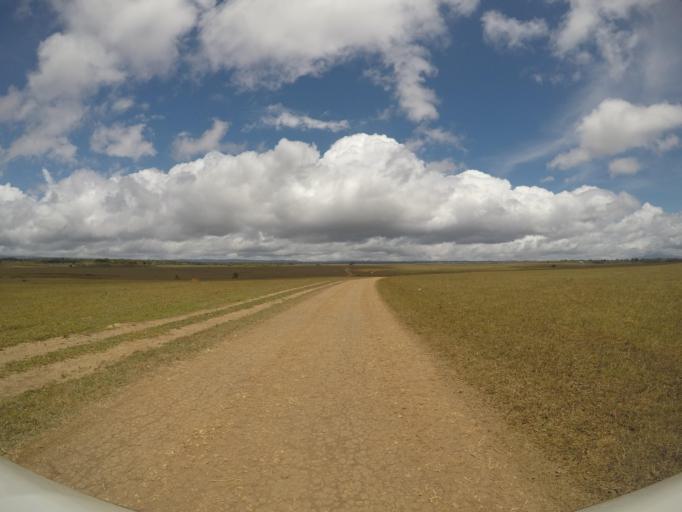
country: TL
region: Lautem
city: Lospalos
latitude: -8.4564
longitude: 126.9848
